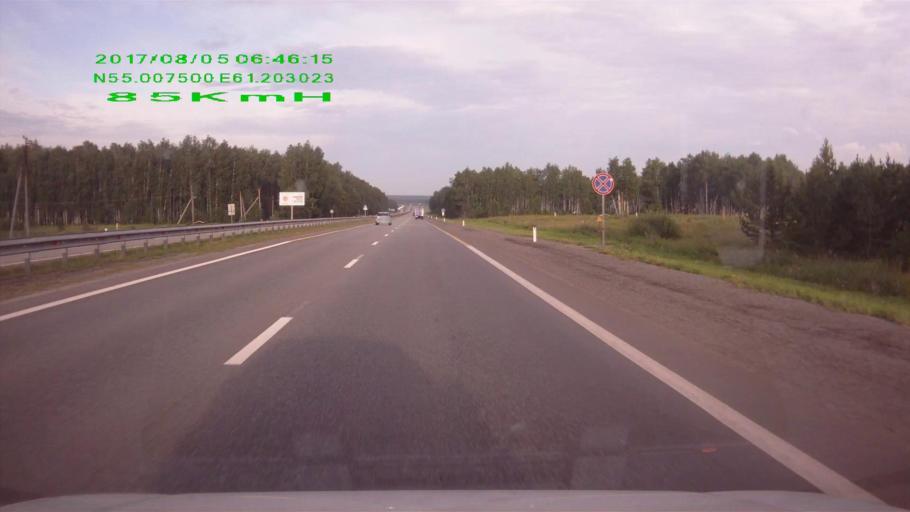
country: RU
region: Chelyabinsk
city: Sargazy
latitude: 55.0074
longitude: 61.2022
